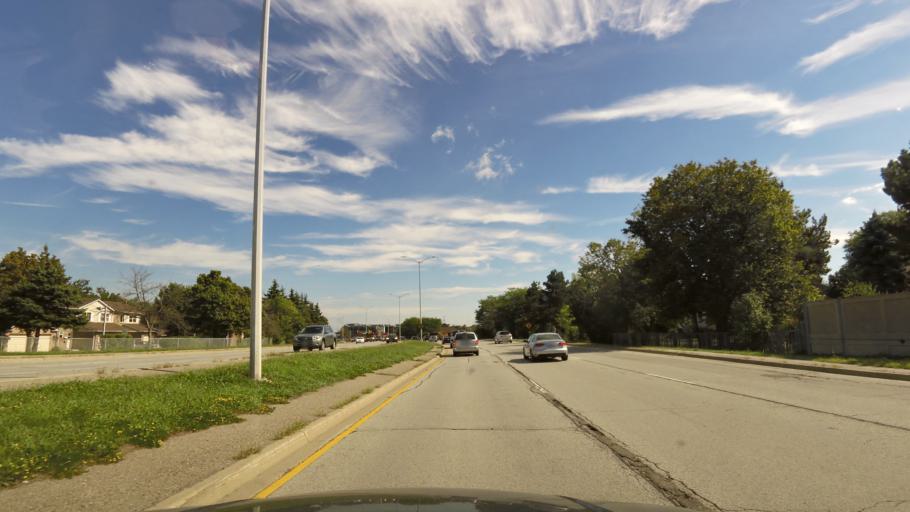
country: CA
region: Ontario
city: Mississauga
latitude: 43.5421
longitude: -79.6769
